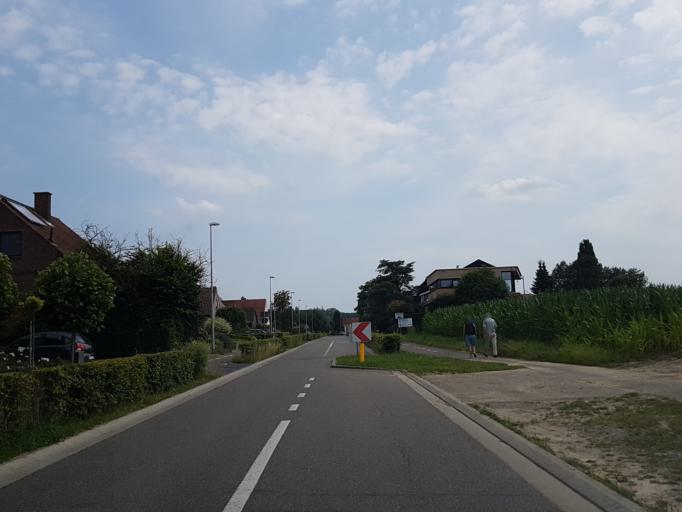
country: BE
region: Flanders
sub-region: Provincie Vlaams-Brabant
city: Herent
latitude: 50.9064
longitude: 4.6438
